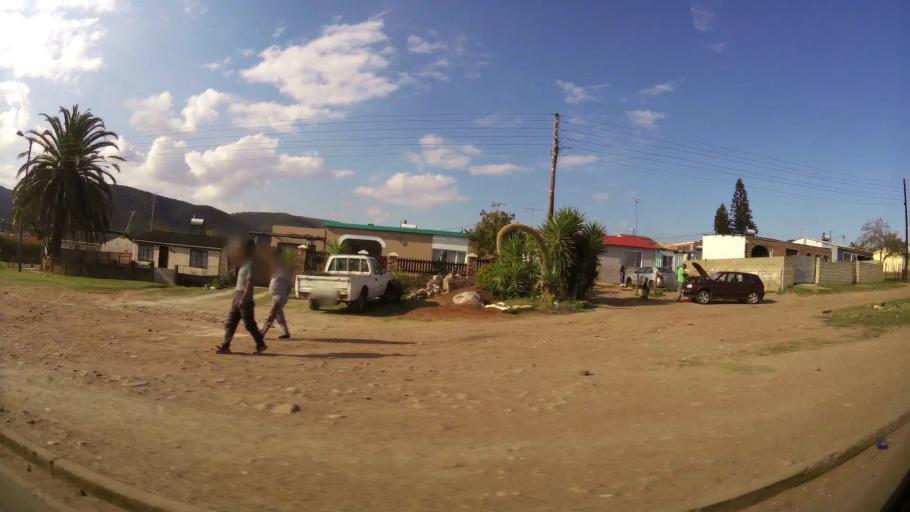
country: ZA
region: Eastern Cape
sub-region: Nelson Mandela Bay Metropolitan Municipality
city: Uitenhage
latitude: -33.7342
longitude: 25.3688
